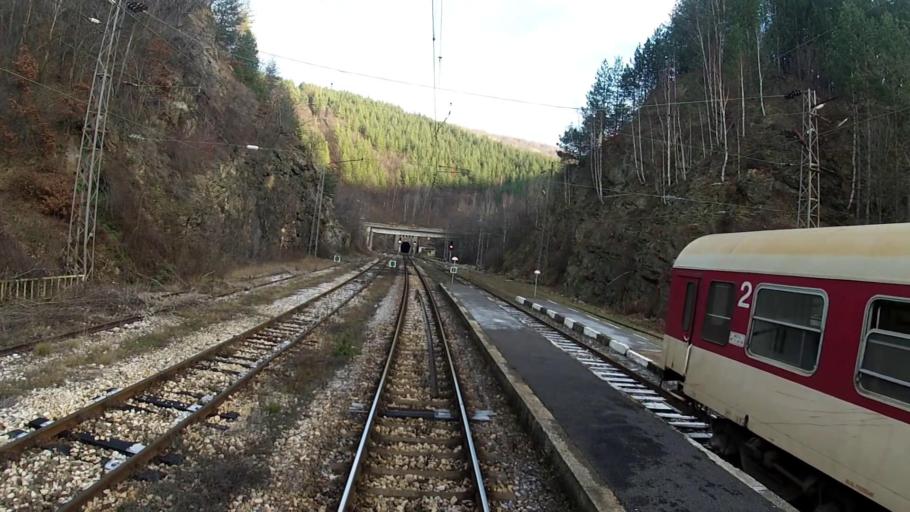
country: BG
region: Sofiya
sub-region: Obshtina Koprivshtitsa
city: Koprivshtitsa
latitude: 42.7009
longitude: 24.3398
